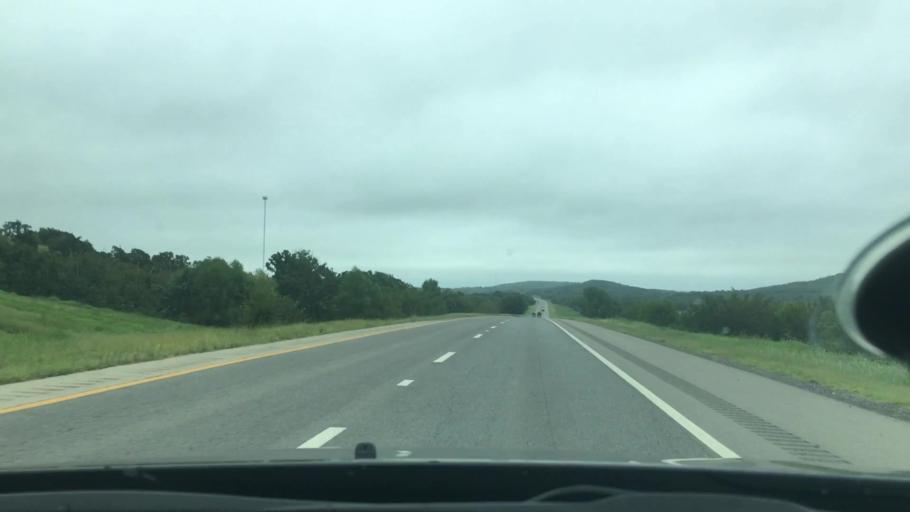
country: US
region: Oklahoma
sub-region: McIntosh County
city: Checotah
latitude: 35.4572
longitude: -95.4234
